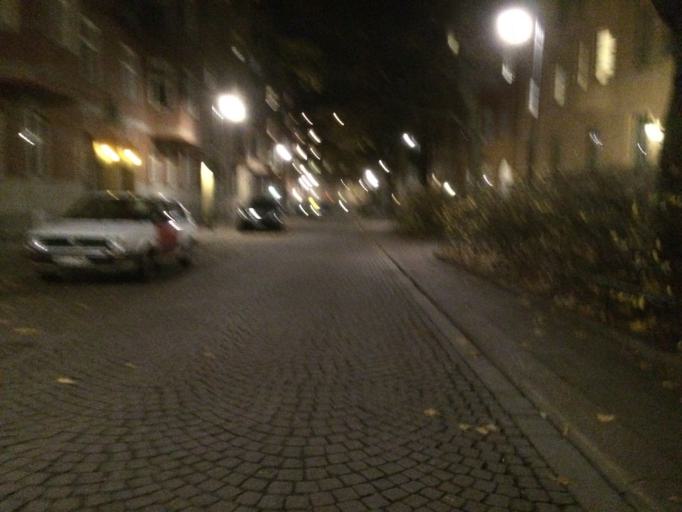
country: SE
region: Stockholm
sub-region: Stockholms Kommun
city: OEstermalm
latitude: 59.3381
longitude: 18.0918
